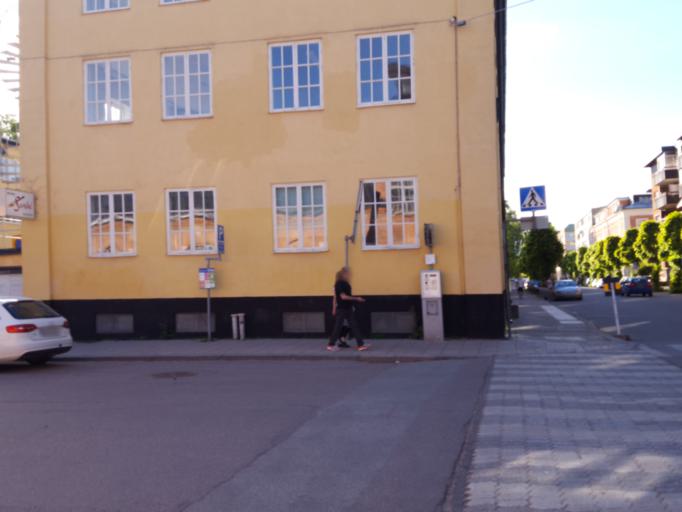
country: SE
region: Uppsala
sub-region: Uppsala Kommun
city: Uppsala
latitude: 59.8617
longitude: 17.6430
